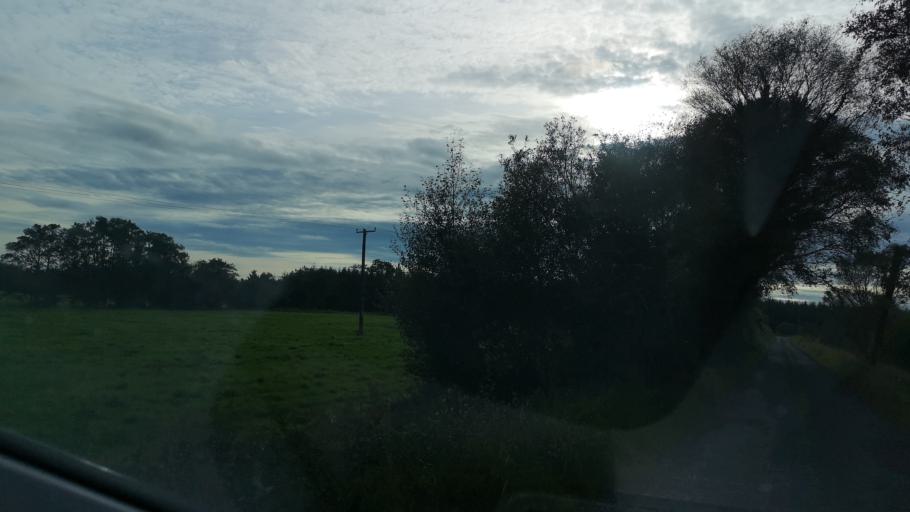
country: IE
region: Connaught
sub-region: County Galway
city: Ballinasloe
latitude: 53.3430
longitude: -8.2918
